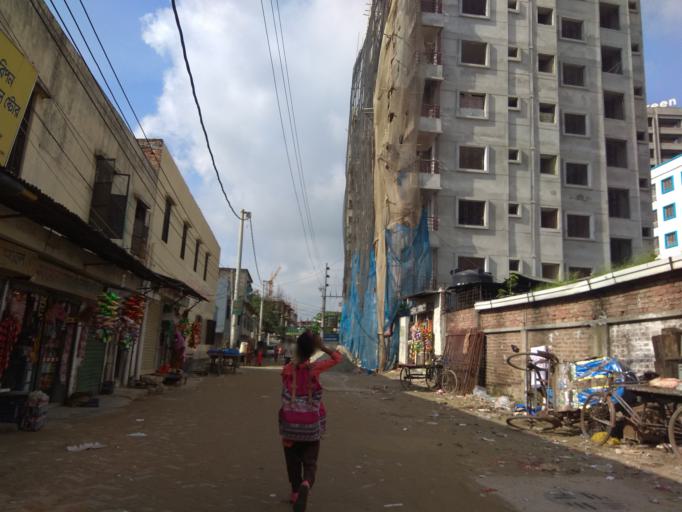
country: BD
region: Dhaka
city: Paltan
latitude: 23.8079
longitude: 90.3837
